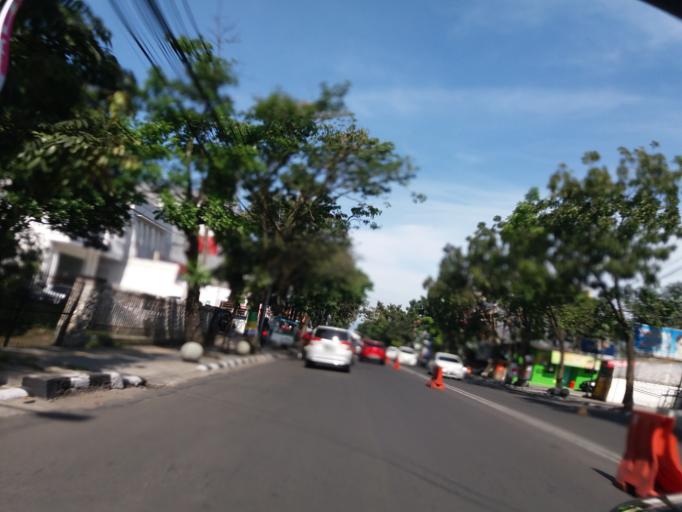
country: ID
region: West Java
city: Bandung
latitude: -6.9386
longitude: 107.6244
